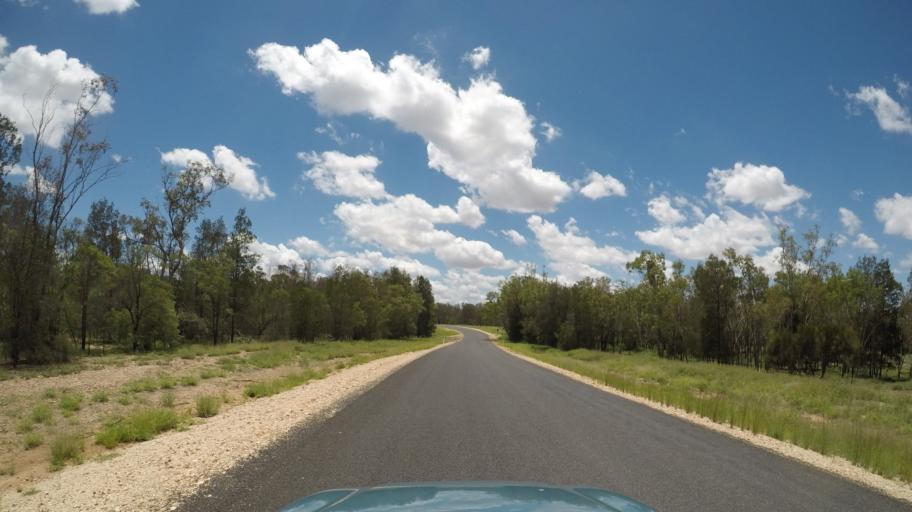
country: AU
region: Queensland
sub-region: Goondiwindi
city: Goondiwindi
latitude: -28.1506
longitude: 150.1266
